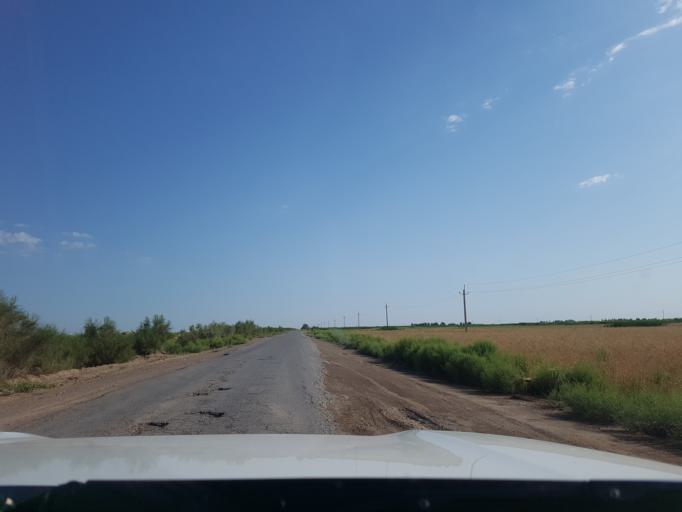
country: TM
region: Dasoguz
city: Koeneuergench
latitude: 41.9065
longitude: 58.7090
